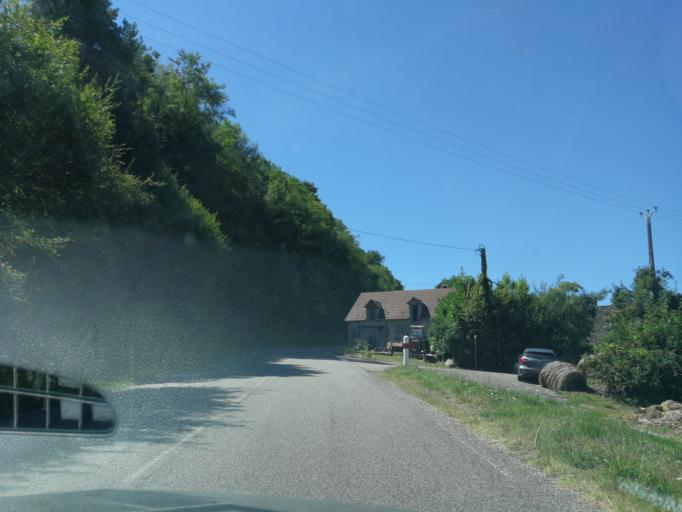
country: FR
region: Limousin
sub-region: Departement de la Correze
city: Argentat
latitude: 45.0819
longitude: 1.9470
